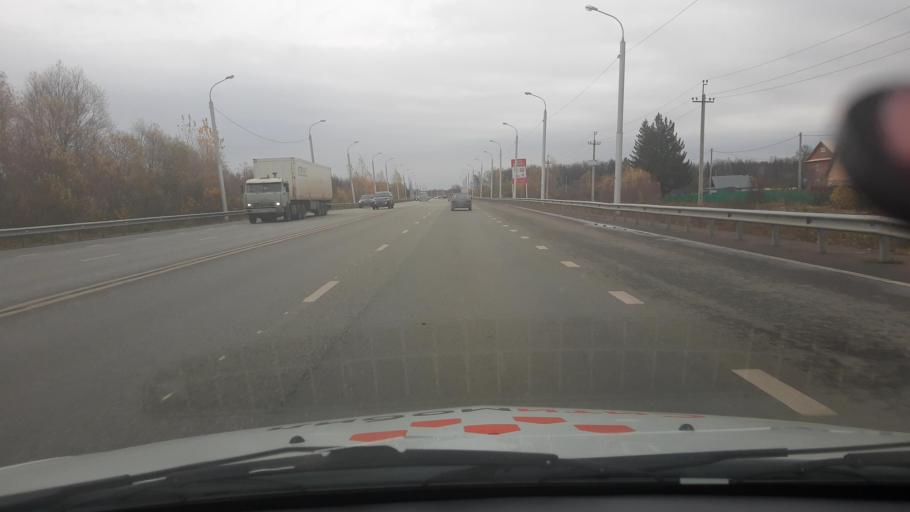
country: RU
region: Bashkortostan
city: Ufa
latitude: 54.8056
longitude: 56.1552
